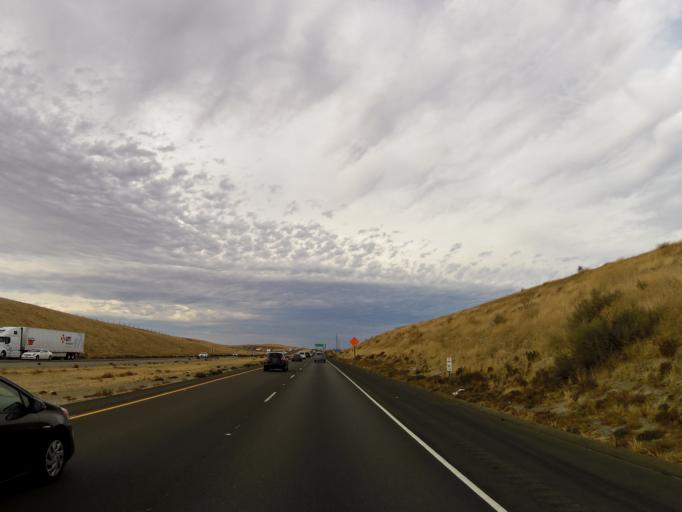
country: US
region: California
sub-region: Kings County
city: Kettleman City
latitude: 35.9749
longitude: -119.9532
